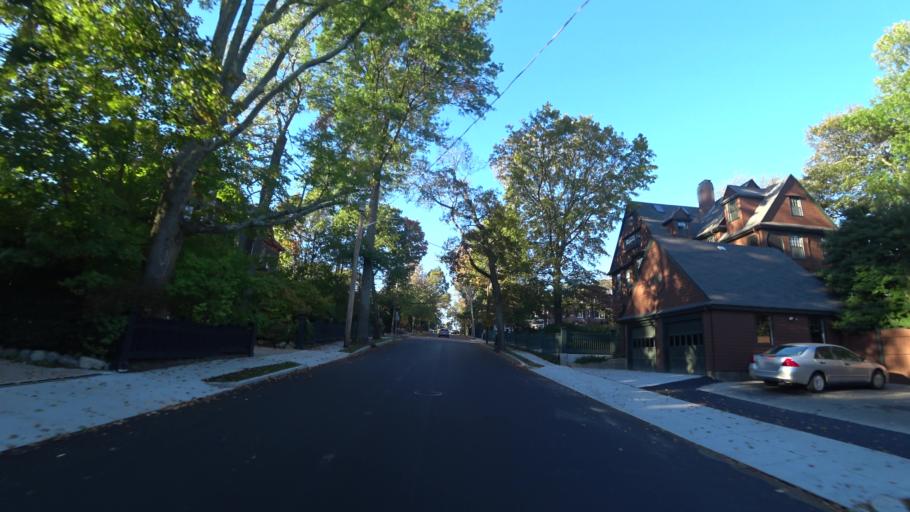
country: US
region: Massachusetts
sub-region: Middlesex County
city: Cambridge
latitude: 42.3785
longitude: -71.1337
